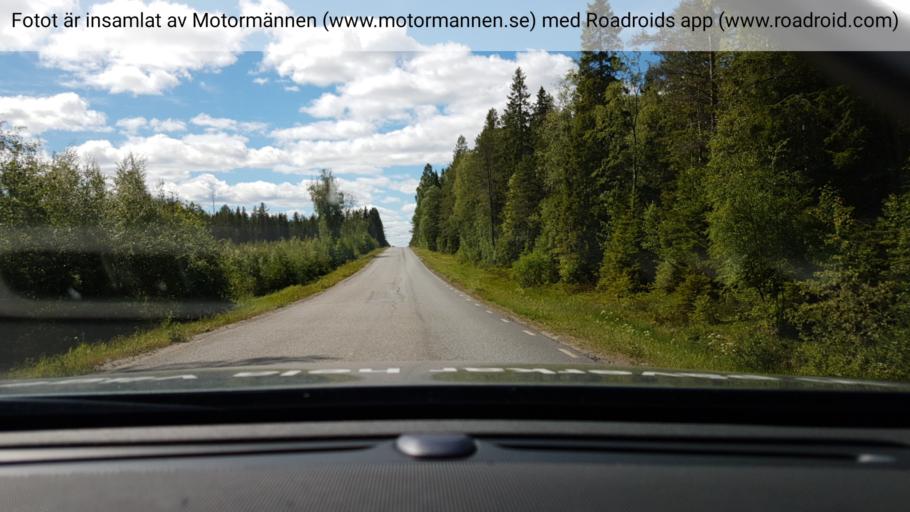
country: SE
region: Vaesterbotten
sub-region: Skelleftea Kommun
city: Burea
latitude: 64.4001
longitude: 21.3396
